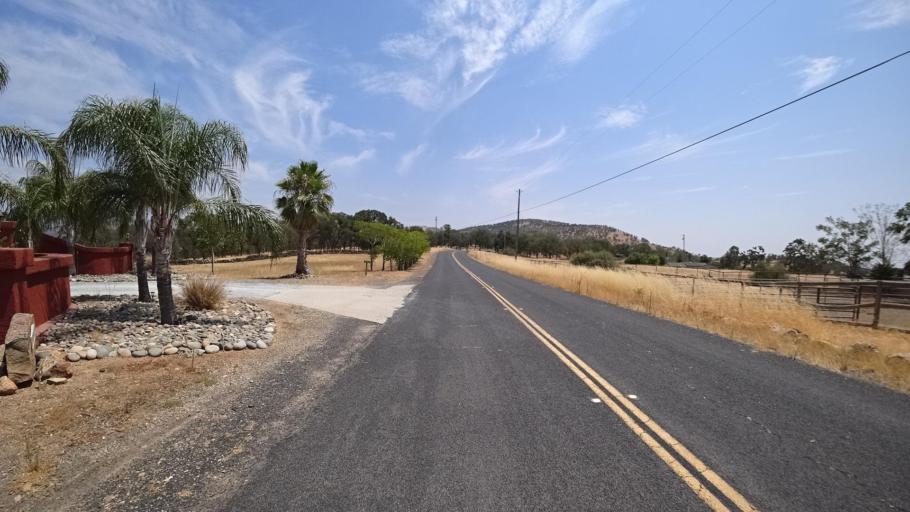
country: US
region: California
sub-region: Tuolumne County
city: Jamestown
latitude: 37.6425
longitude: -120.3259
